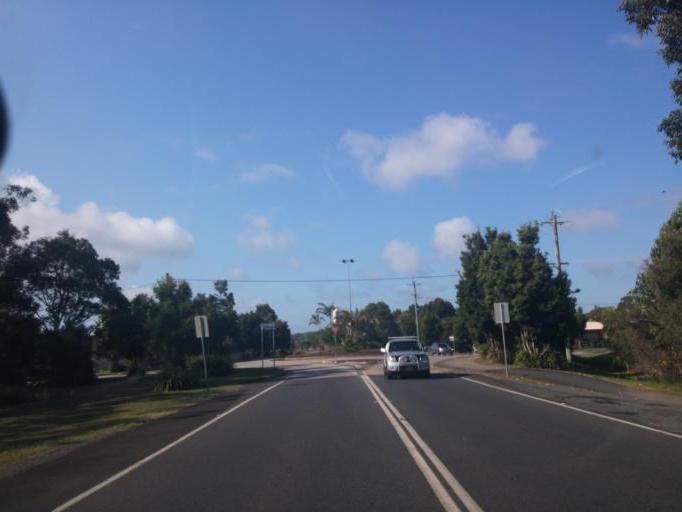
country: AU
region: New South Wales
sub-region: Coffs Harbour
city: Coffs Harbour
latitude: -30.2895
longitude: 153.1349
